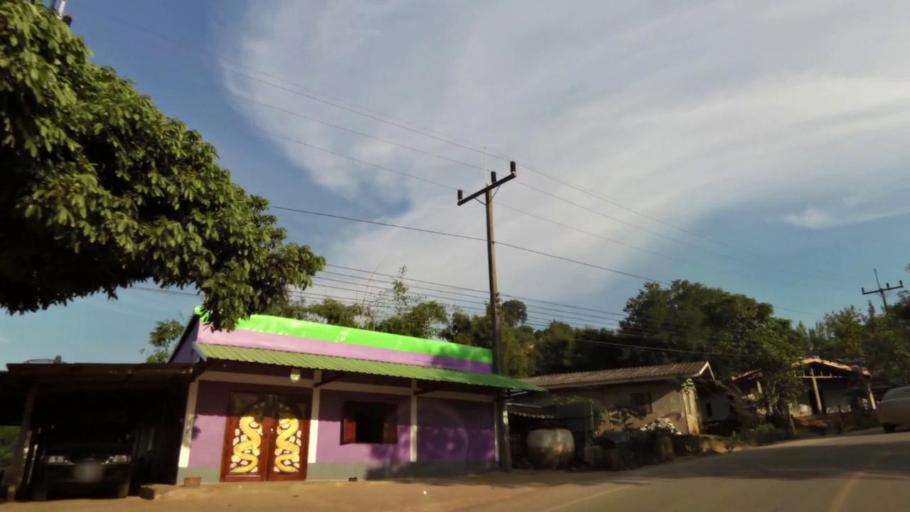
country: TH
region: Chiang Rai
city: Khun Tan
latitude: 19.8687
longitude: 100.4004
